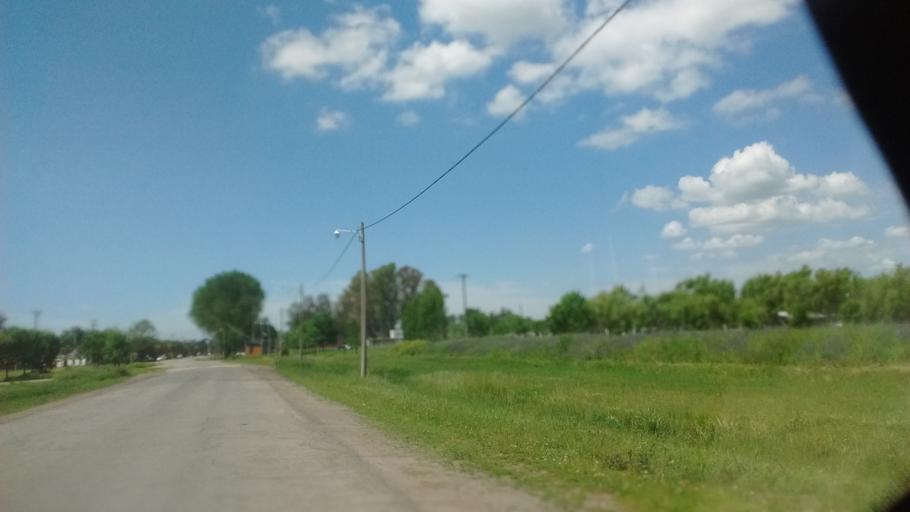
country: AR
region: Santa Fe
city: Funes
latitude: -32.8496
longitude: -60.7932
